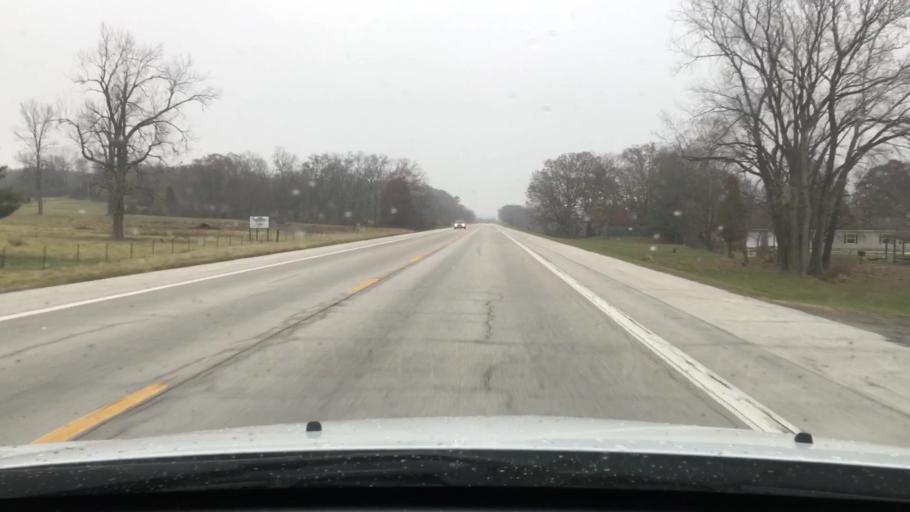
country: US
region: Missouri
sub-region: Pike County
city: Bowling Green
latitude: 39.3733
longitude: -91.1642
